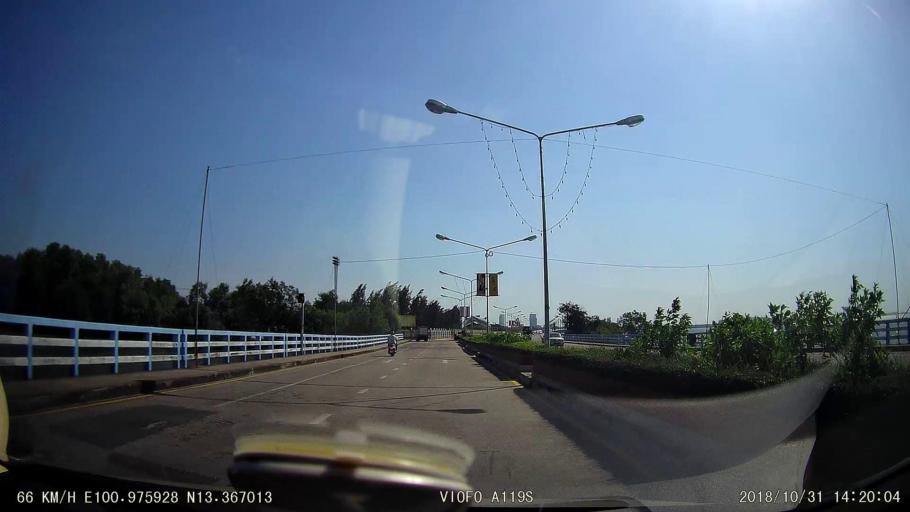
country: TH
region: Chon Buri
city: Chon Buri
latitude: 13.3668
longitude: 100.9759
